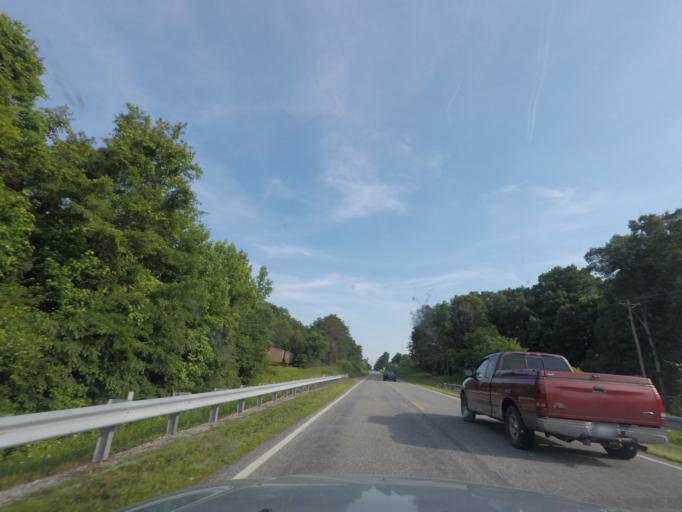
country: US
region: Virginia
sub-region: Mecklenburg County
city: Clarksville
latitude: 36.5583
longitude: -78.5419
